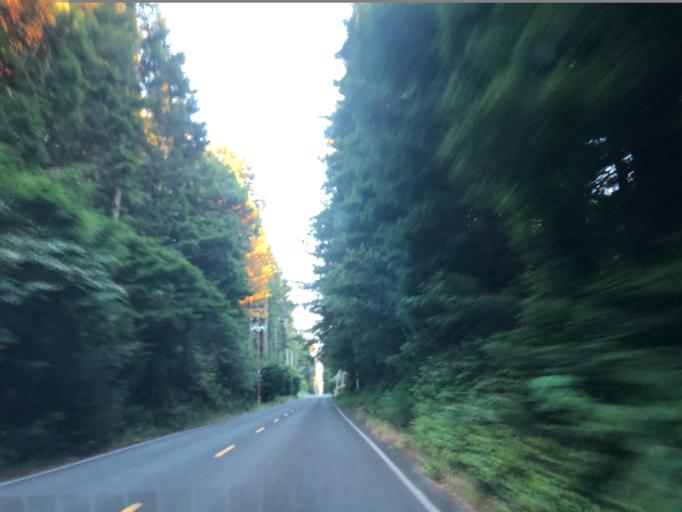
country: US
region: California
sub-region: Humboldt County
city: Westhaven-Moonstone
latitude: 41.0828
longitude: -124.1481
